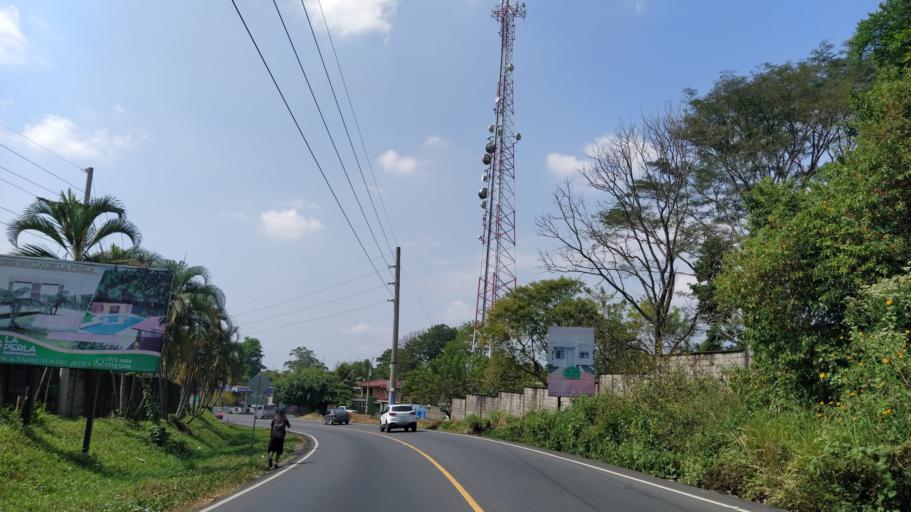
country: GT
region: Retalhuleu
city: San Felipe
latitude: 14.6190
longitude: -91.5970
